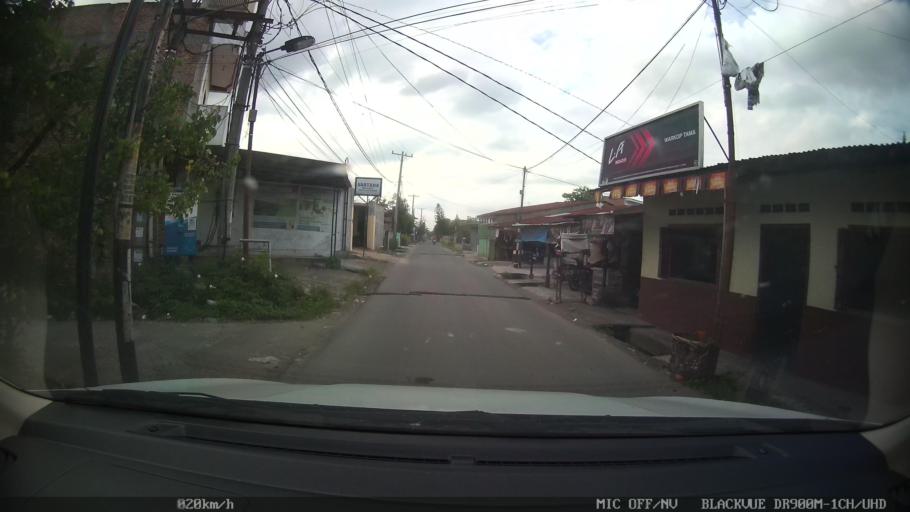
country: ID
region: North Sumatra
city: Sunggal
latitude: 3.6152
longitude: 98.6273
